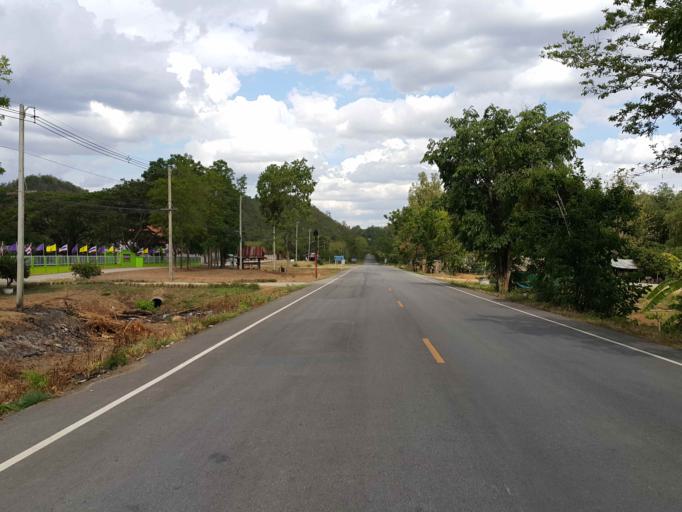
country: TH
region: Sukhothai
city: Thung Saliam
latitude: 17.3456
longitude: 99.4436
